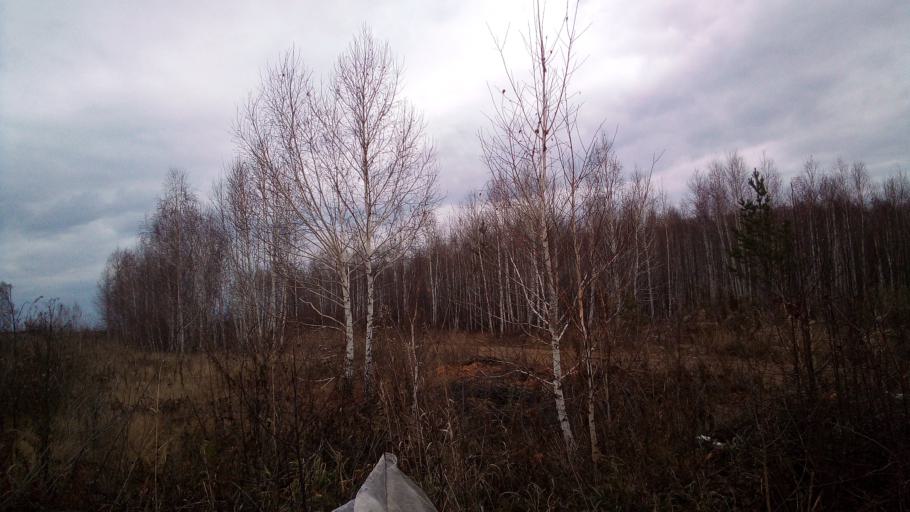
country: RU
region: Chelyabinsk
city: Sargazy
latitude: 55.1250
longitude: 61.2482
